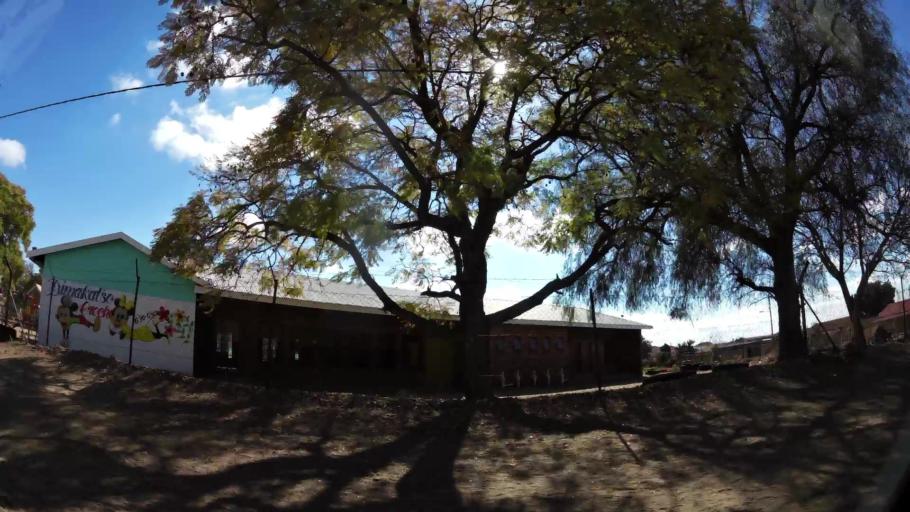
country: ZA
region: Limpopo
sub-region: Capricorn District Municipality
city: Polokwane
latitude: -23.8646
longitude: 29.3892
